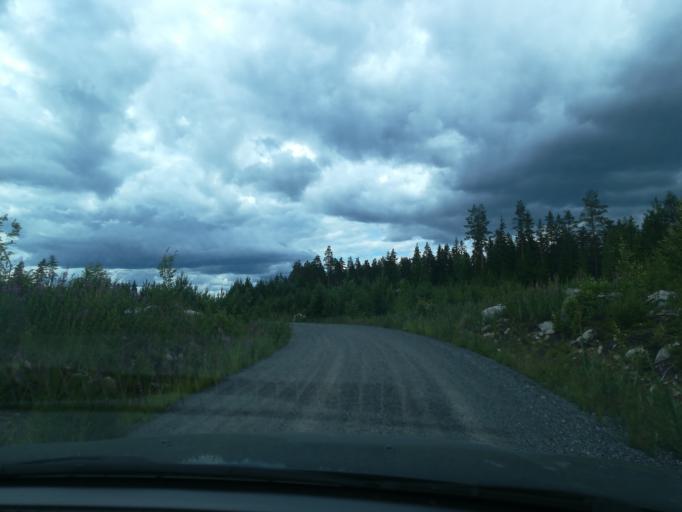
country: FI
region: Southern Savonia
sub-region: Mikkeli
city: Mikkeli
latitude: 61.6686
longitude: 27.1203
